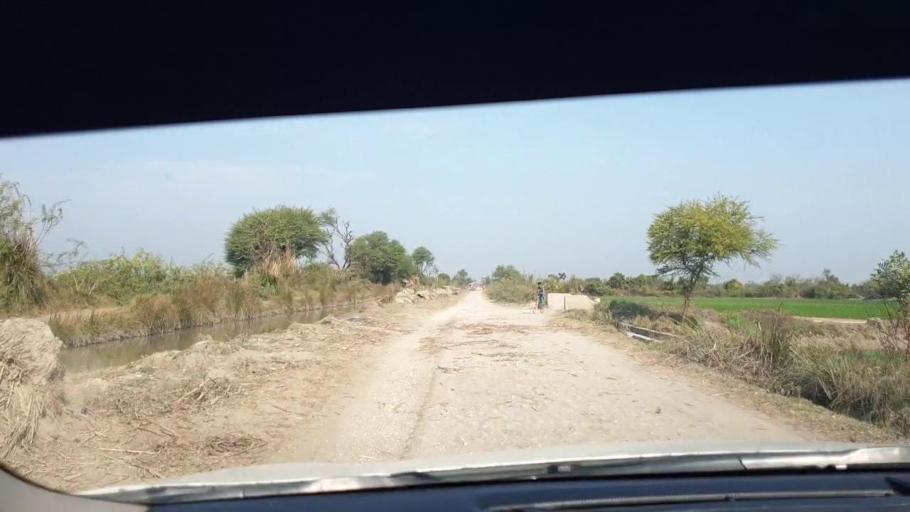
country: PK
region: Sindh
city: Tando Adam
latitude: 25.7326
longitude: 68.7025
